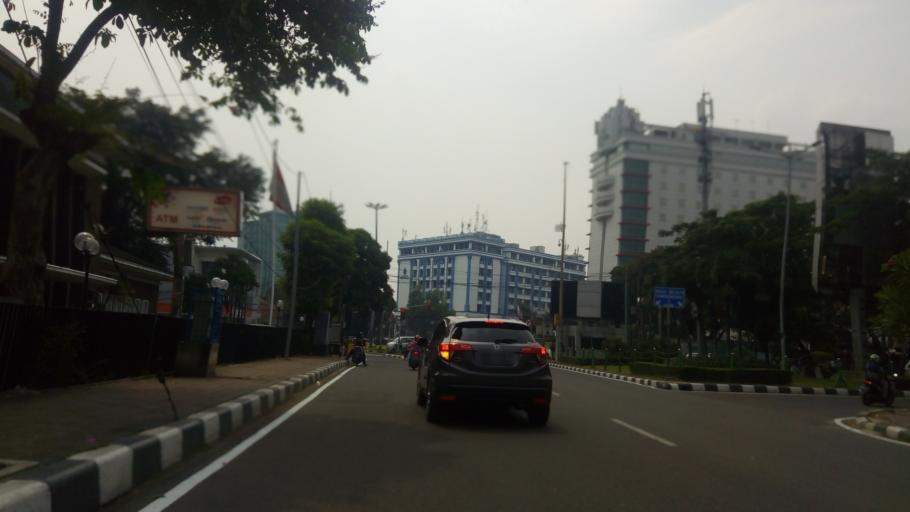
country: ID
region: Jakarta Raya
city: Jakarta
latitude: -6.1878
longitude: 106.8361
